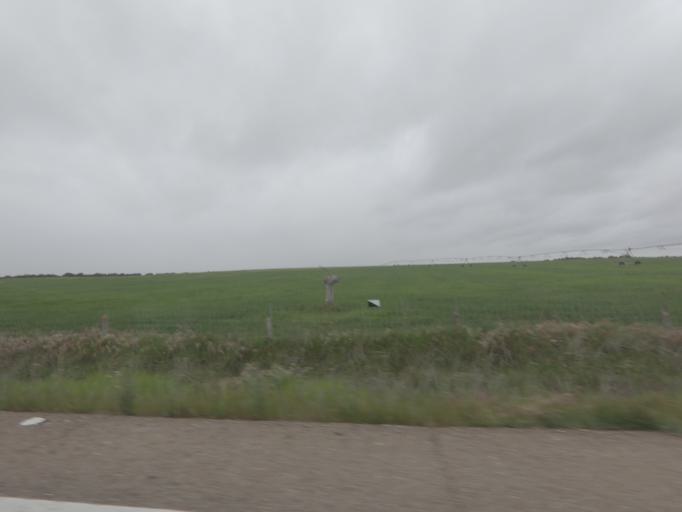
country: ES
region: Extremadura
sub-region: Provincia de Badajoz
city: Badajoz
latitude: 38.9618
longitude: -6.9016
